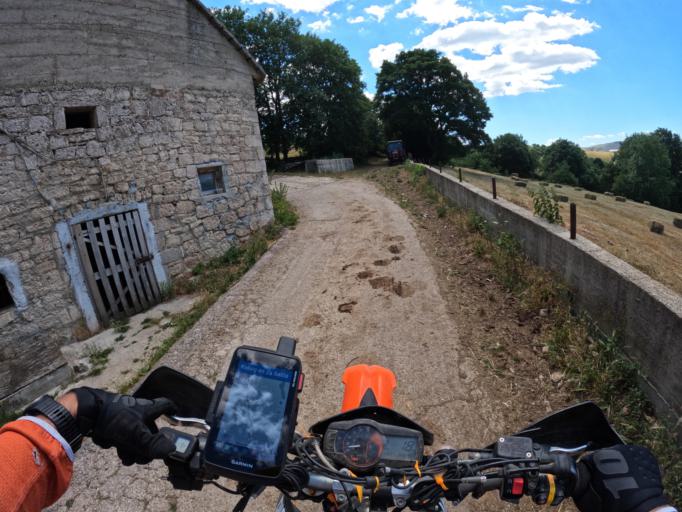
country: BA
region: Federation of Bosnia and Herzegovina
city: Tomislavgrad
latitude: 43.8372
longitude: 17.1932
